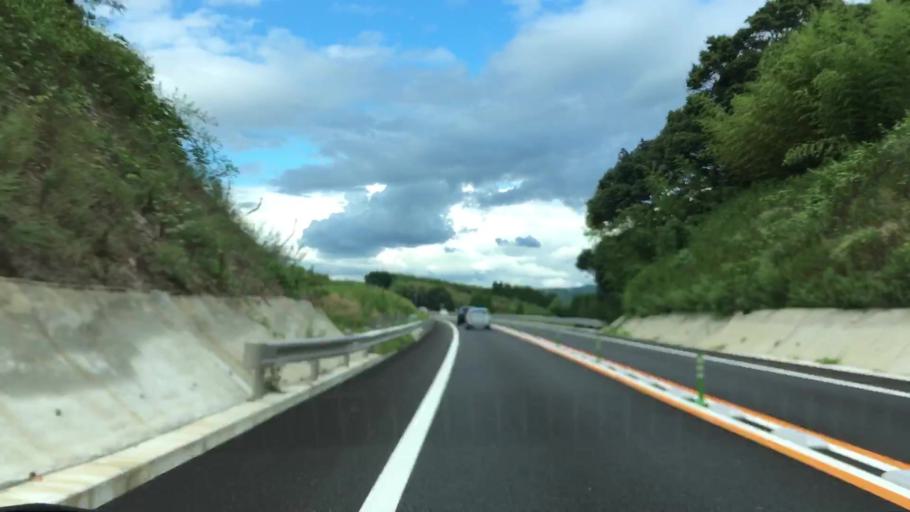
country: JP
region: Saga Prefecture
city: Imaricho-ko
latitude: 33.3175
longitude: 129.9231
